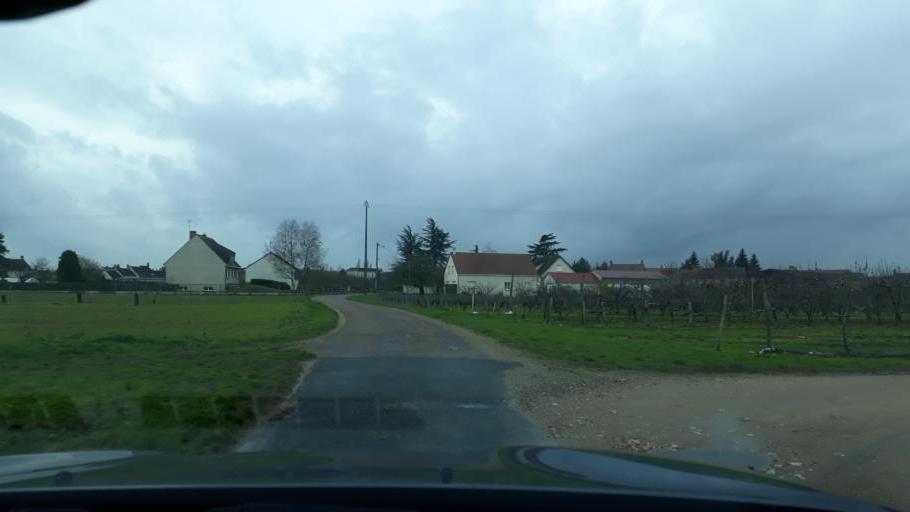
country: FR
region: Centre
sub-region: Departement du Loiret
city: Saint-Hilaire-Saint-Mesmin
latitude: 47.8440
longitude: 1.8175
